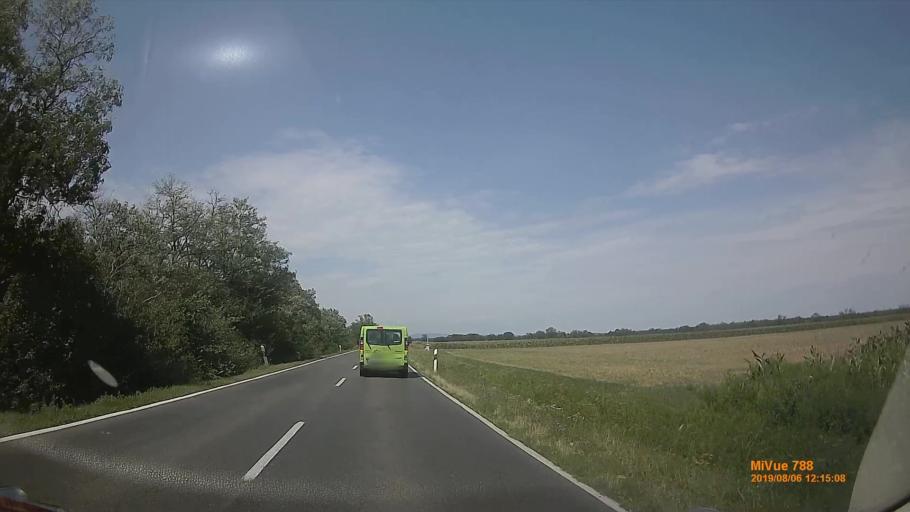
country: HU
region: Vas
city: Vasvar
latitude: 47.1464
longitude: 16.8225
